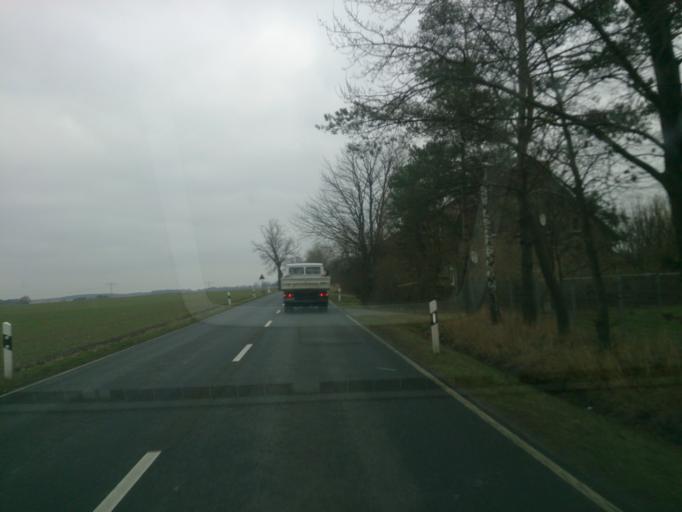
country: DE
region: Mecklenburg-Vorpommern
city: Borrentin
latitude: 53.8260
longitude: 12.9825
